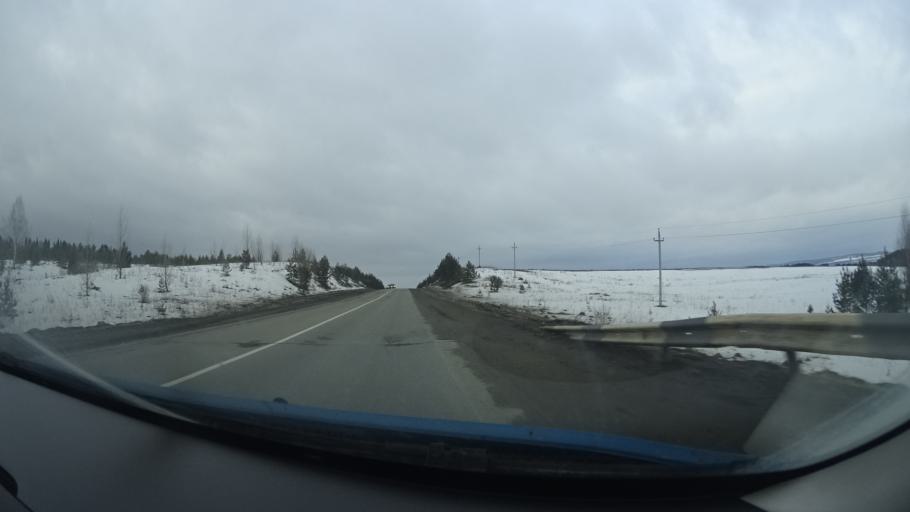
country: RU
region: Perm
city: Osa
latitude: 57.2362
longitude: 55.5950
